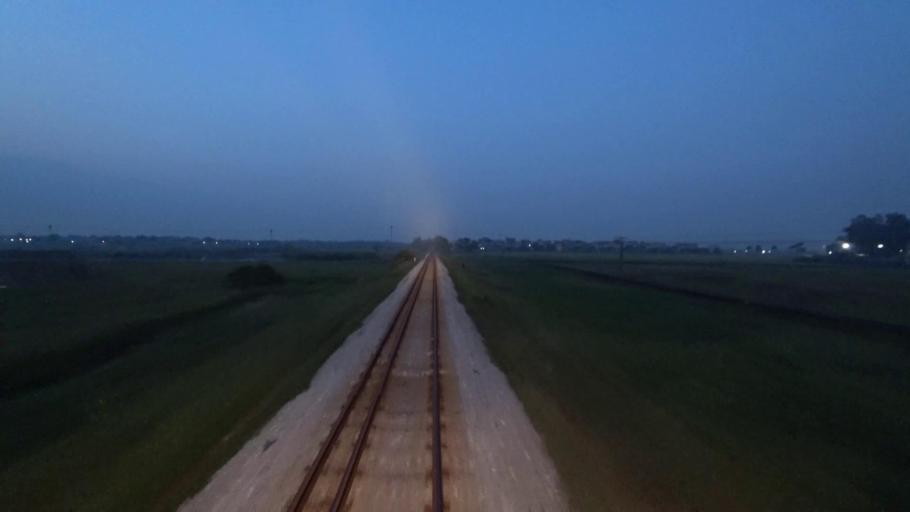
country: VN
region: Ha Noi
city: Soc Son
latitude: 21.2646
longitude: 105.8621
